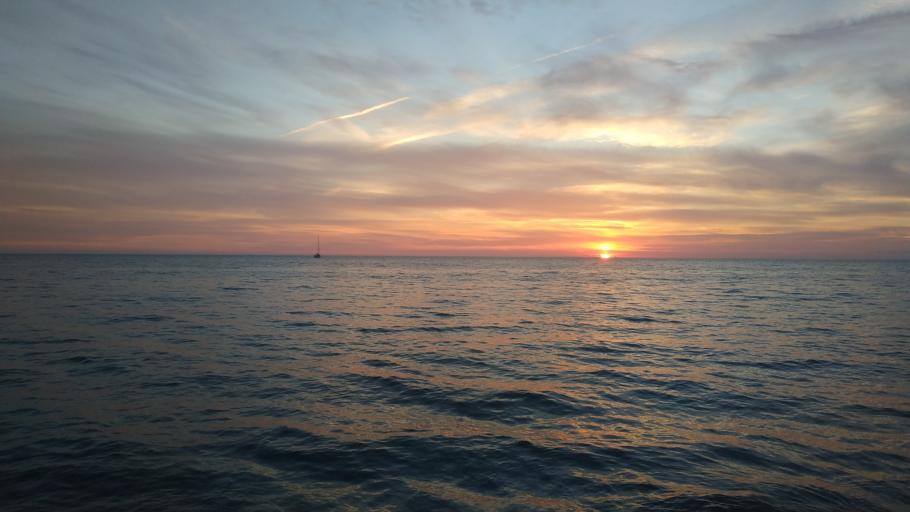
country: RU
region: Krasnodarskiy
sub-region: Sochi City
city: Lazarevskoye
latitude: 43.9170
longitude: 39.3172
